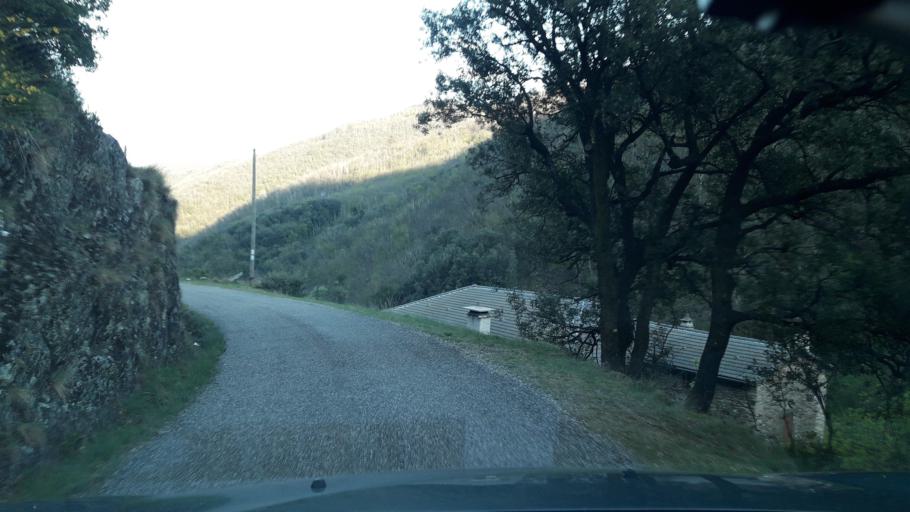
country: FR
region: Languedoc-Roussillon
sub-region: Departement du Gard
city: Valleraugue
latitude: 44.1077
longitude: 3.6617
